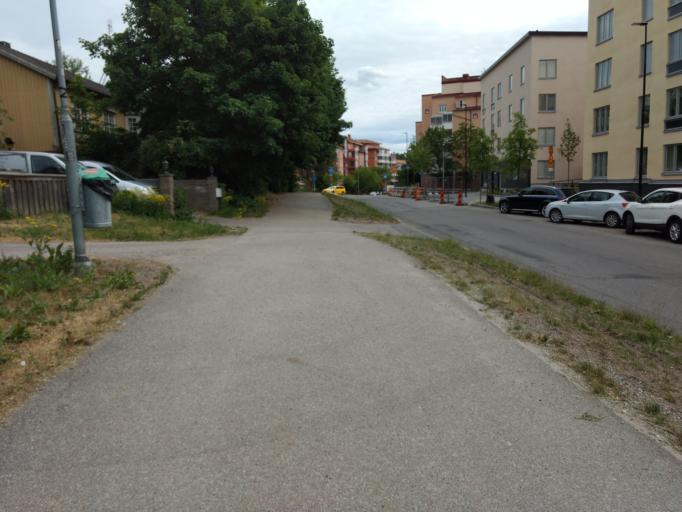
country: SE
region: Stockholm
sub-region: Upplands Vasby Kommun
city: Upplands Vaesby
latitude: 59.5236
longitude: 17.9042
